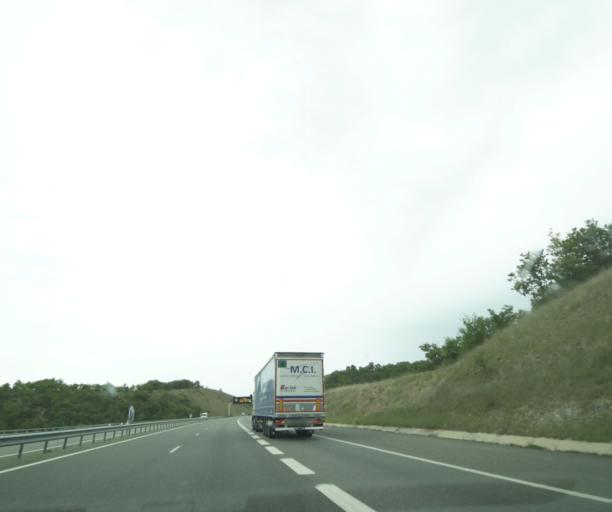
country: FR
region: Midi-Pyrenees
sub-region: Departement du Lot
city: Cahors
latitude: 44.4863
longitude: 1.4982
